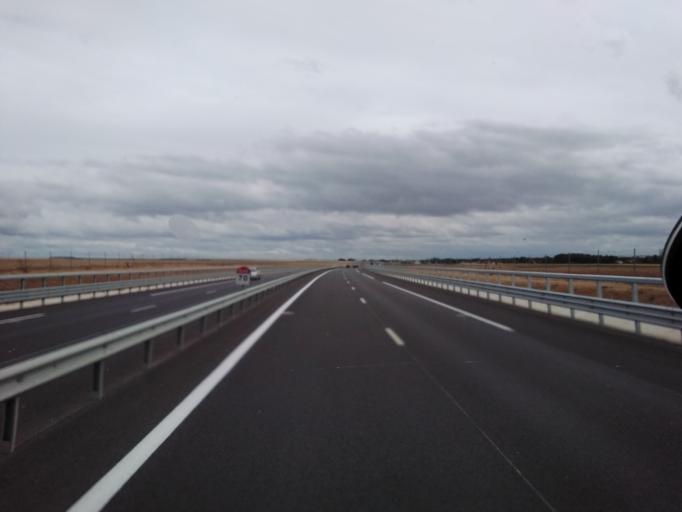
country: FR
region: Champagne-Ardenne
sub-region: Departement de la Marne
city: Sarry
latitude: 48.9009
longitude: 4.4486
